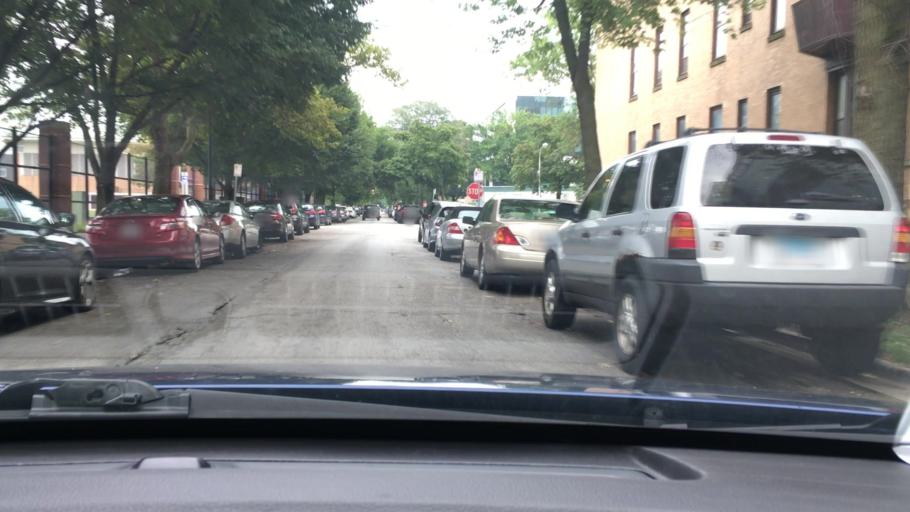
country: US
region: Illinois
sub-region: Cook County
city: Chicago
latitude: 41.7932
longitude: -87.6045
